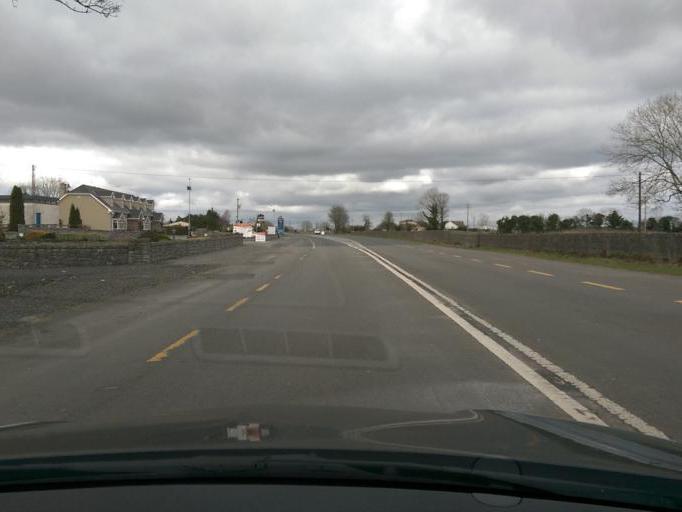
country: IE
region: Connaught
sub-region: County Galway
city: Ballinasloe
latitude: 53.3466
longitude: -8.0904
